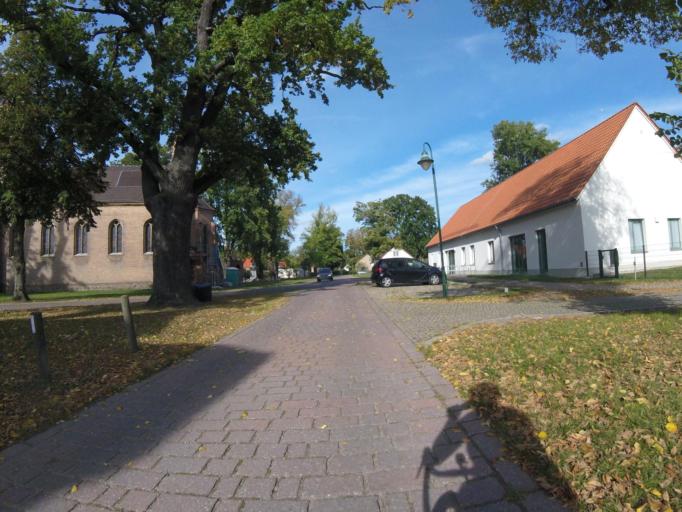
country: DE
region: Brandenburg
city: Bestensee
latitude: 52.2930
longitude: 13.7200
